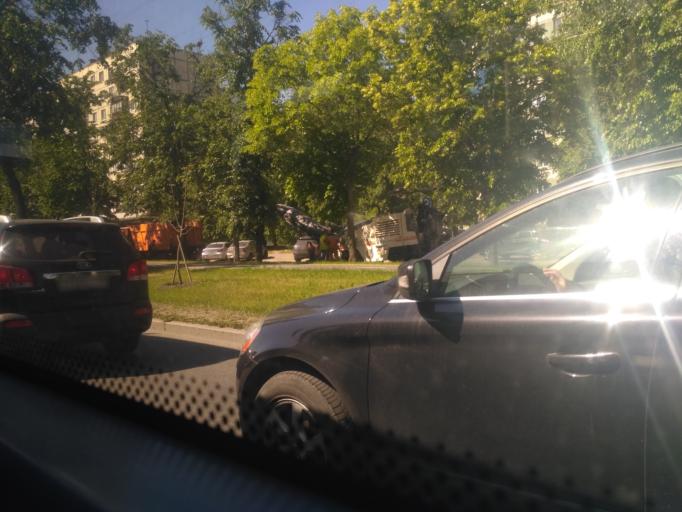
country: RU
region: Leningrad
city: Kalininskiy
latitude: 59.9714
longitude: 30.4119
